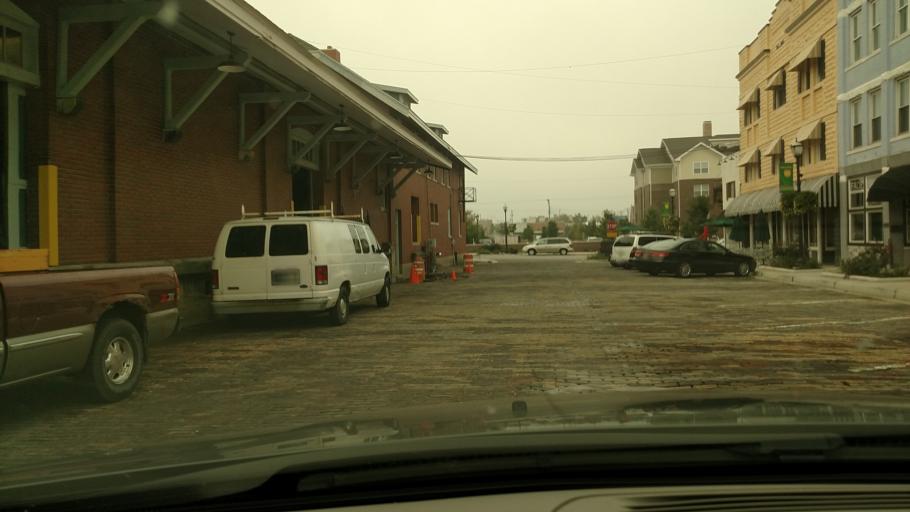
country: US
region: Indiana
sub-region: Howard County
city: Kokomo
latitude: 40.4904
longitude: -86.1329
